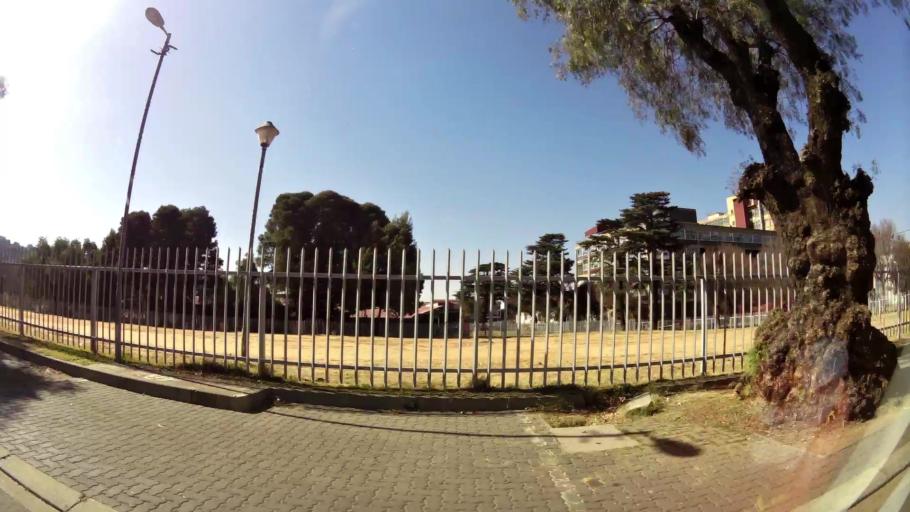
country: ZA
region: Gauteng
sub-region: City of Johannesburg Metropolitan Municipality
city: Johannesburg
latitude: -26.1972
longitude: 28.0636
